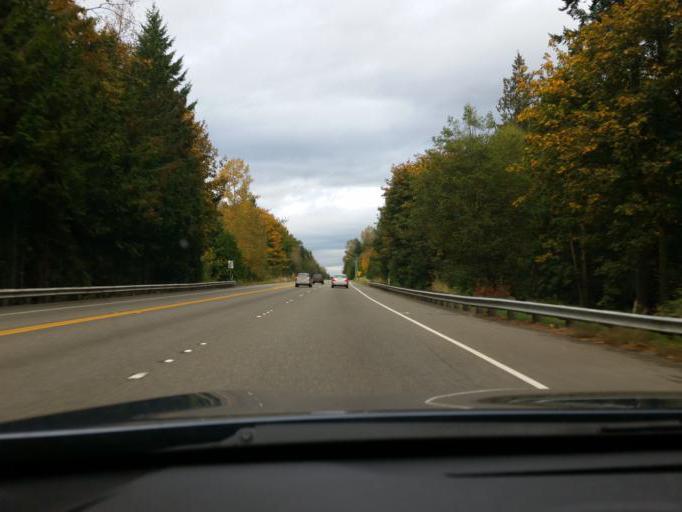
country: US
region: Washington
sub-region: Snohomish County
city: West Lake Stevens
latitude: 47.9926
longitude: -122.1251
